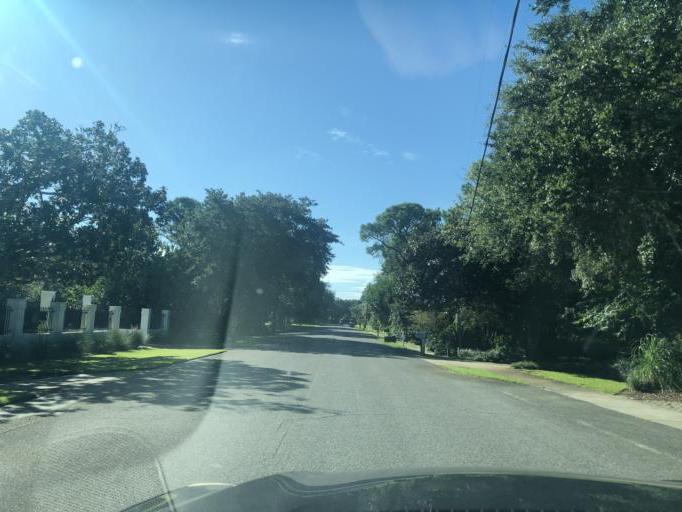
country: US
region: Florida
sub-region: Okaloosa County
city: Destin
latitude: 30.4080
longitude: -86.5004
